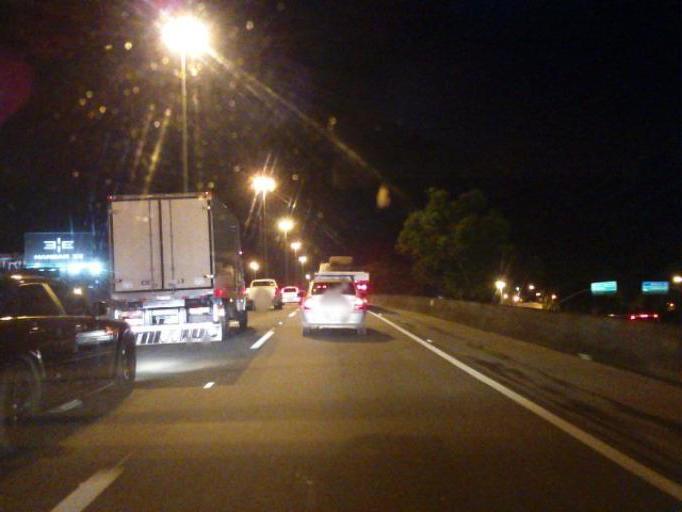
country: BR
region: Santa Catarina
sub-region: Balneario Camboriu
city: Balneario Camboriu
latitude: -26.9988
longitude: -48.6477
